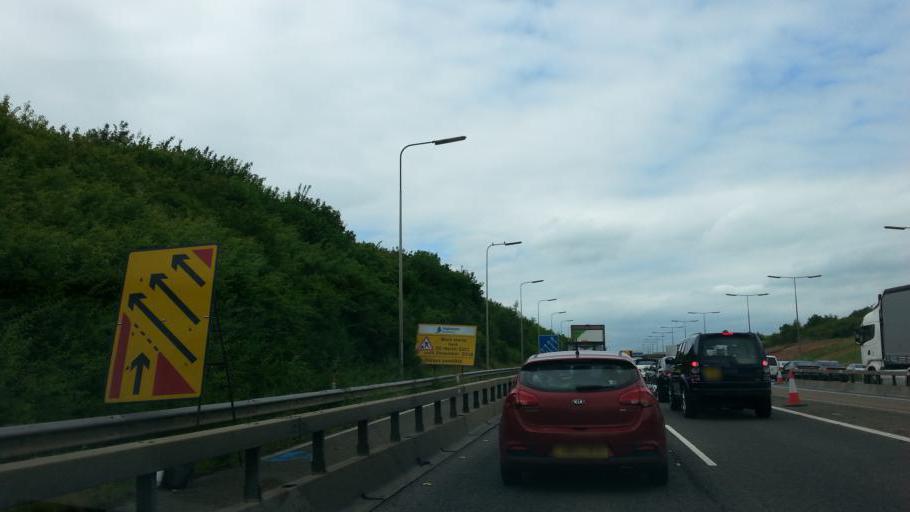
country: GB
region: England
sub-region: Leicestershire
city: Kegworth
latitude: 52.8181
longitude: -1.3061
